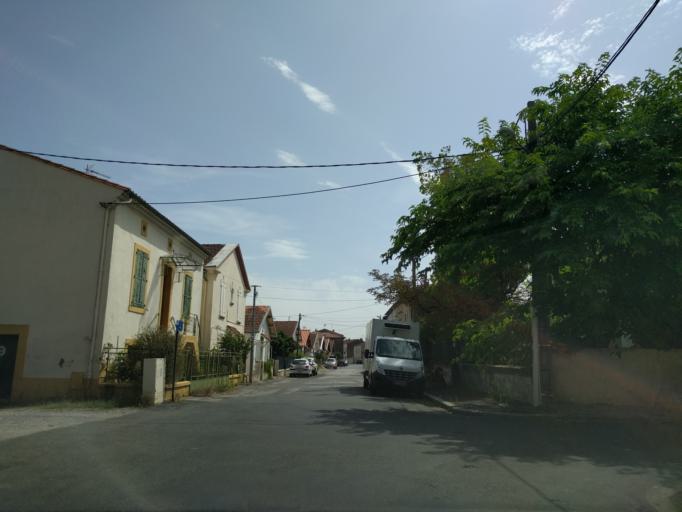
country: FR
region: Midi-Pyrenees
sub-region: Departement du Tarn
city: Castres
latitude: 43.6100
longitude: 2.2301
